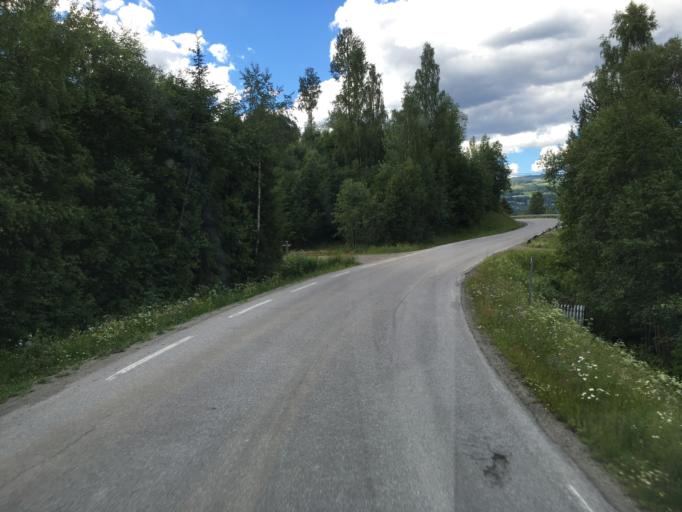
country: NO
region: Oppland
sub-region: Nordre Land
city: Dokka
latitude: 60.8160
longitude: 10.0870
